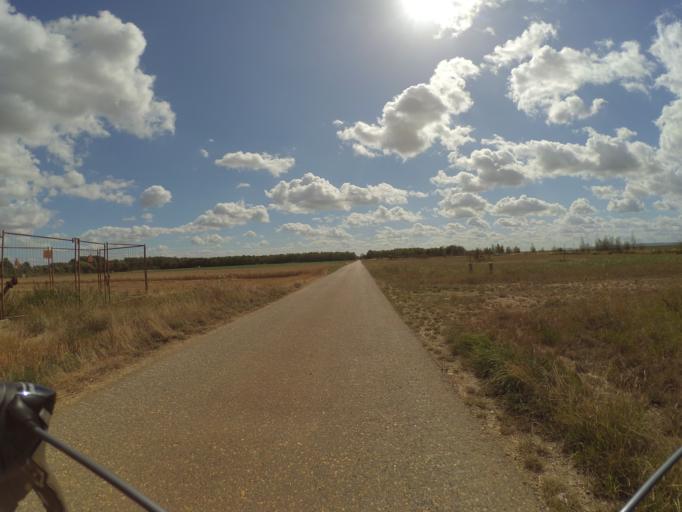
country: DE
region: North Rhine-Westphalia
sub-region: Regierungsbezirk Koln
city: Inden
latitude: 50.8822
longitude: 6.3838
